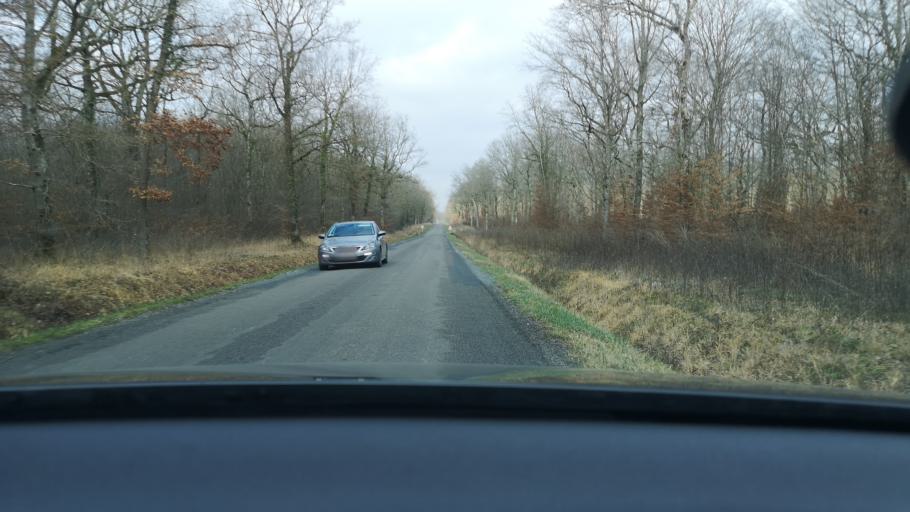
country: FR
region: Bourgogne
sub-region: Departement de Saone-et-Loire
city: Dracy-le-Fort
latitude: 46.7653
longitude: 4.7721
